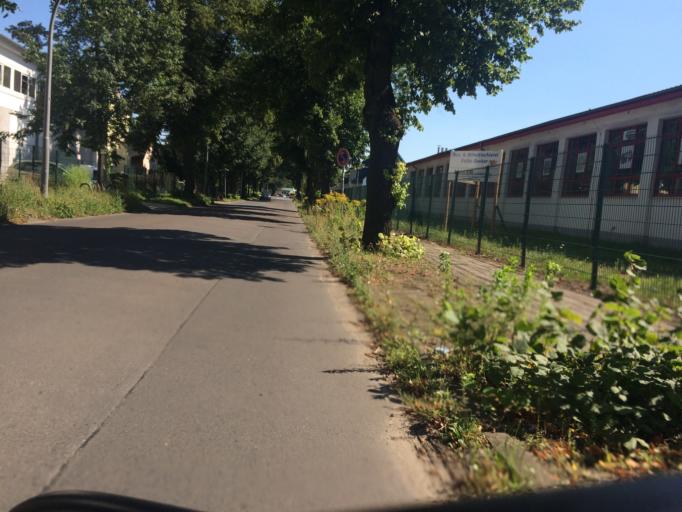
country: DE
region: Berlin
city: Buchholz
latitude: 52.5938
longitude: 13.4288
